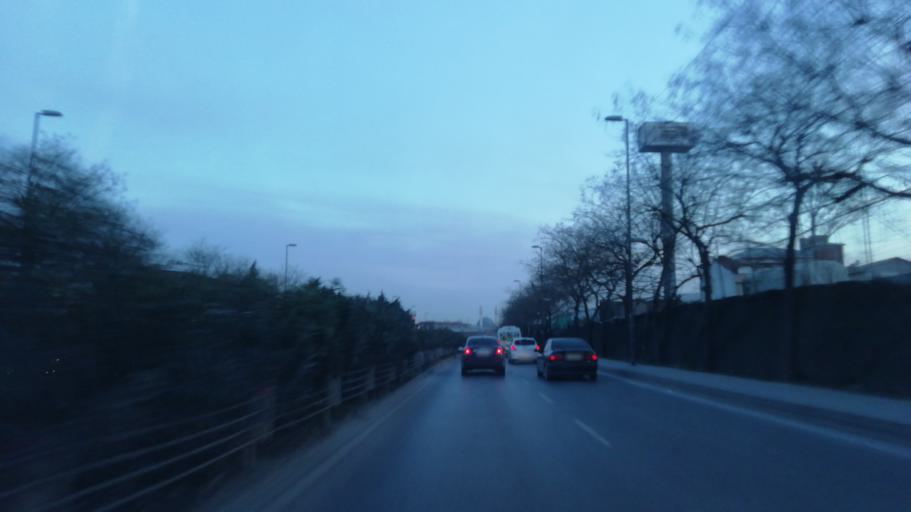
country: TR
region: Istanbul
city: Bagcilar
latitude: 41.0209
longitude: 28.8485
